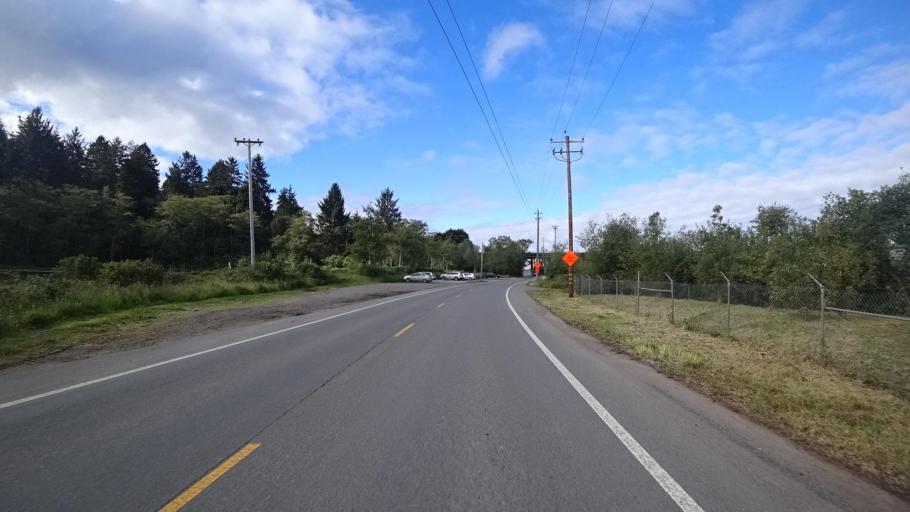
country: US
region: California
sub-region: Humboldt County
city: Arcata
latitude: 40.8931
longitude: -124.0792
